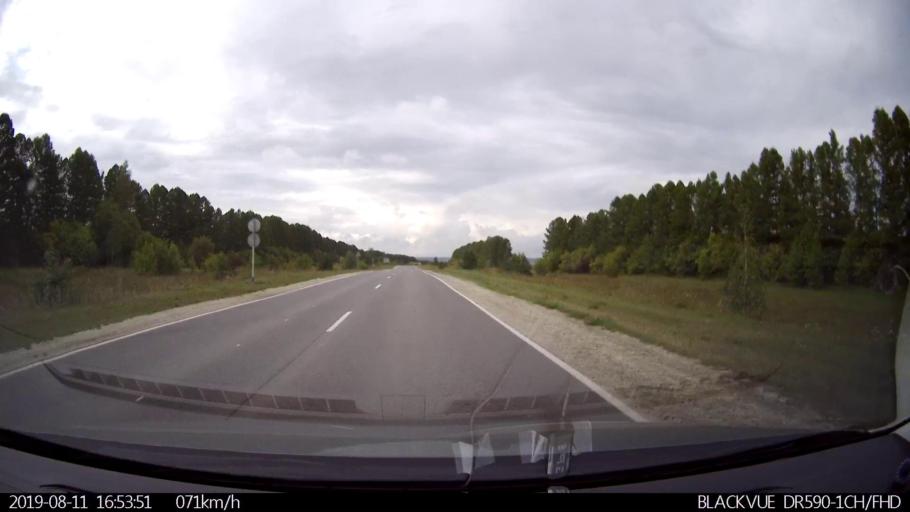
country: RU
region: Ulyanovsk
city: Mayna
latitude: 54.2670
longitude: 47.6685
